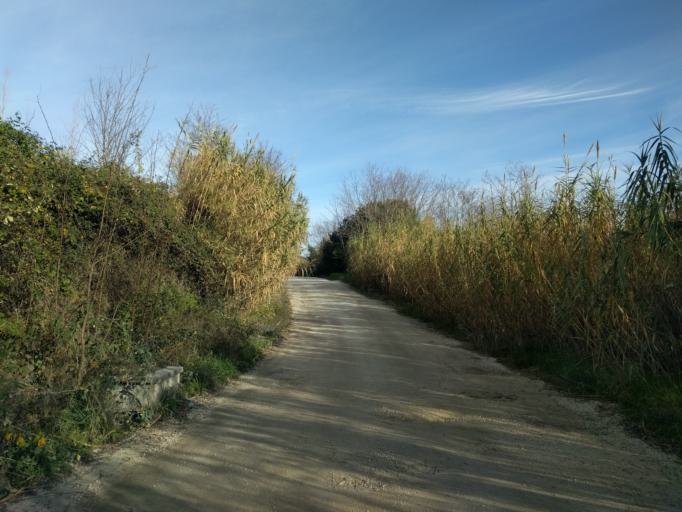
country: IT
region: The Marches
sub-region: Provincia di Pesaro e Urbino
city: Cuccurano
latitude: 43.8098
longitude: 12.9634
